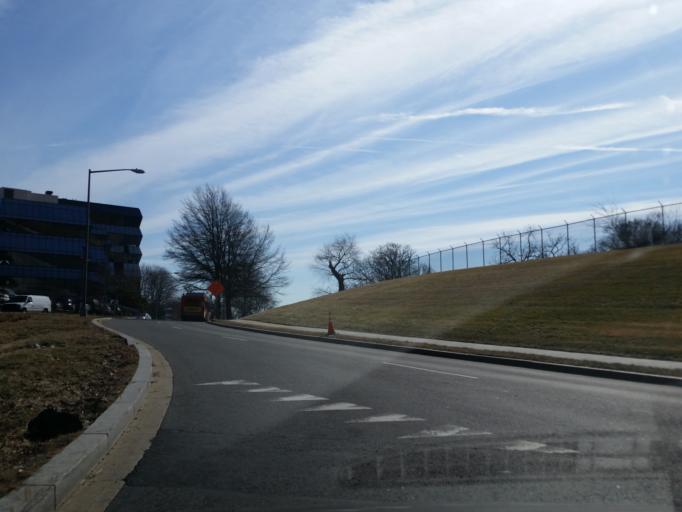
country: US
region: Washington, D.C.
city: Washington, D.C.
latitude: 38.9281
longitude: -77.0179
